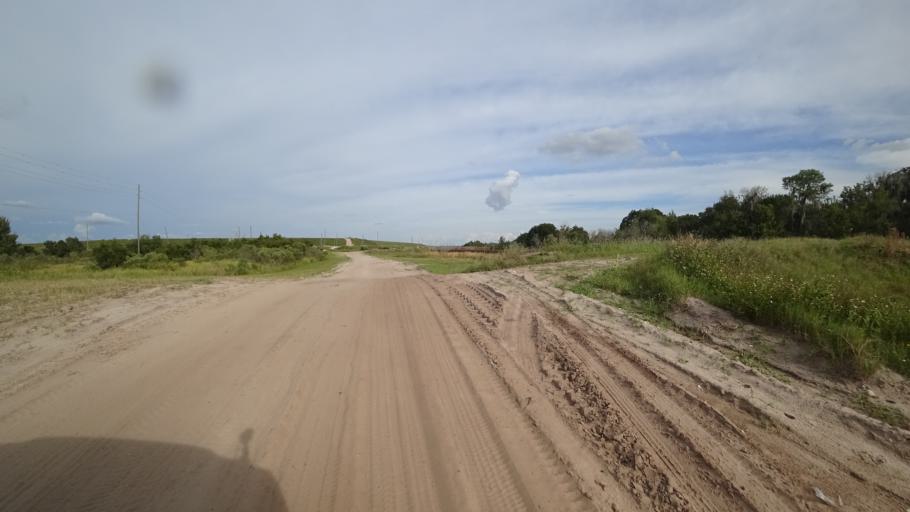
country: US
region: Florida
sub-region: Hardee County
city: Wauchula
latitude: 27.5299
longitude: -82.0713
